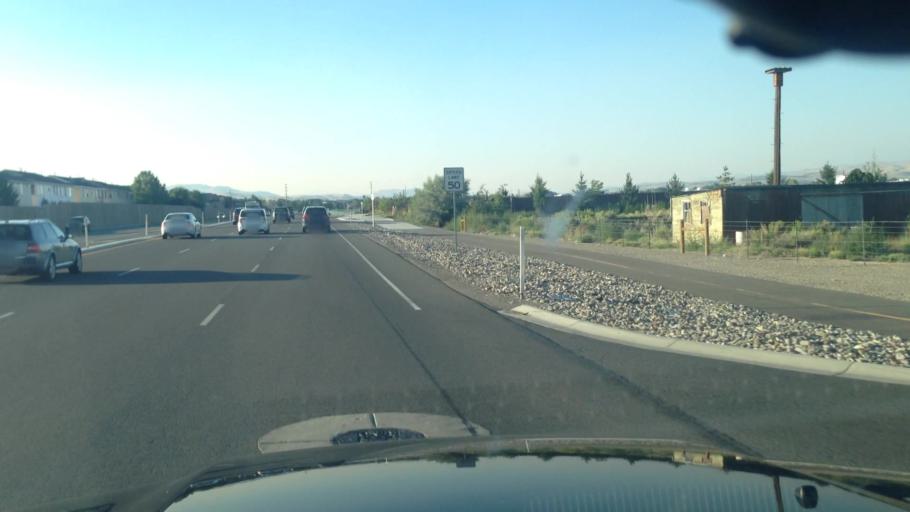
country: US
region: Nevada
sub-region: Washoe County
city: Sparks
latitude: 39.4978
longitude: -119.7480
